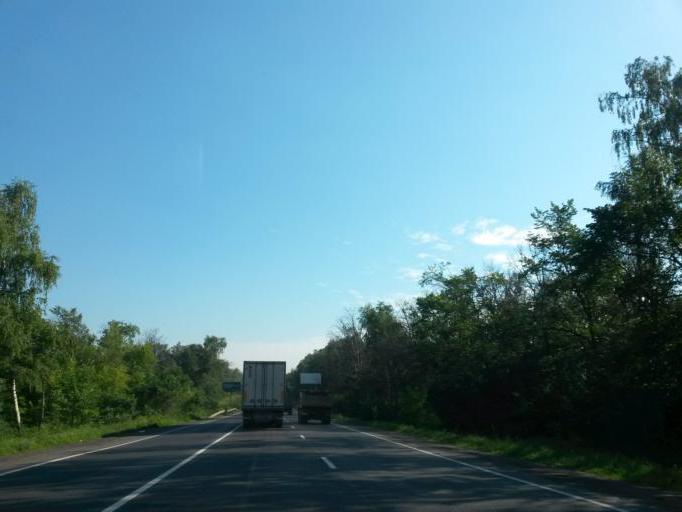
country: RU
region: Moskovskaya
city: Gorki-Leninskiye
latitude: 55.5221
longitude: 37.7635
